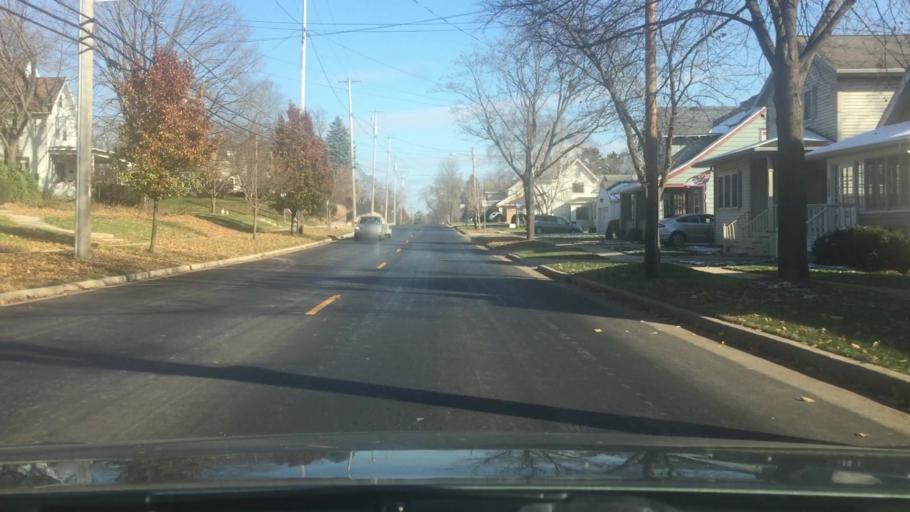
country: US
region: Wisconsin
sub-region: Jefferson County
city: Fort Atkinson
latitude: 42.9299
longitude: -88.8329
